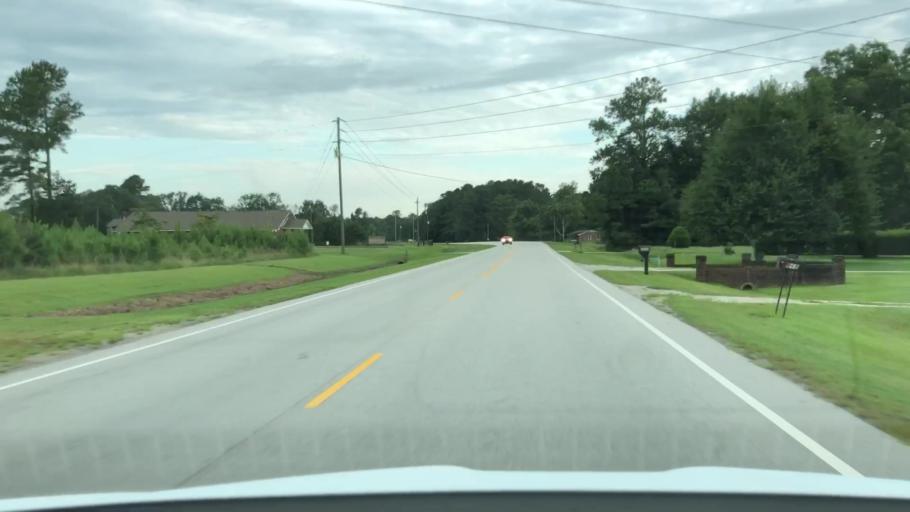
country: US
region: North Carolina
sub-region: Jones County
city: Trenton
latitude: 35.0270
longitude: -77.3087
